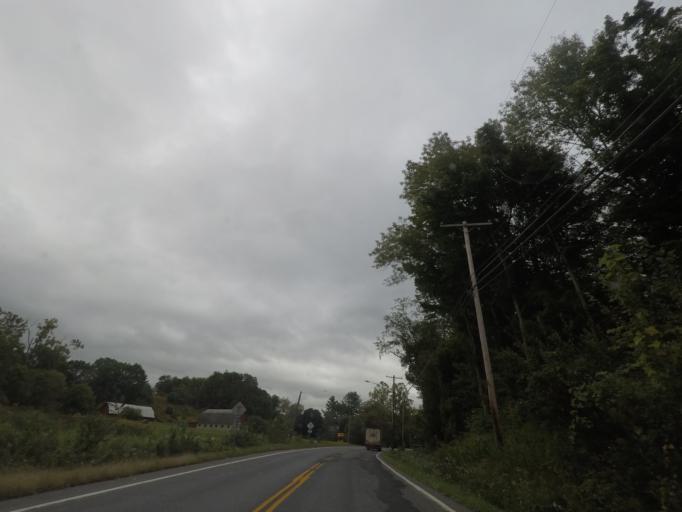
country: US
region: New York
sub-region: Rensselaer County
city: Hoosick Falls
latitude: 42.9311
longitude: -73.3543
